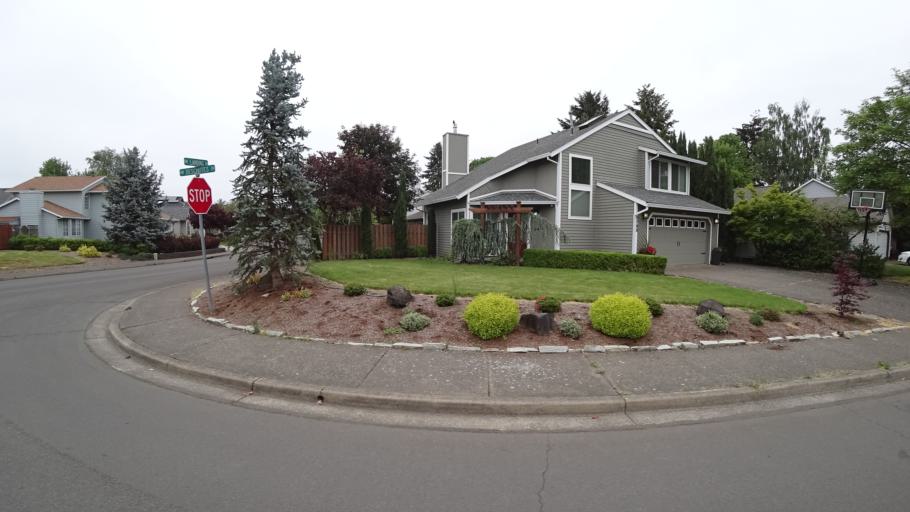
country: US
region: Oregon
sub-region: Washington County
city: Rockcreek
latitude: 45.5618
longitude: -122.8941
